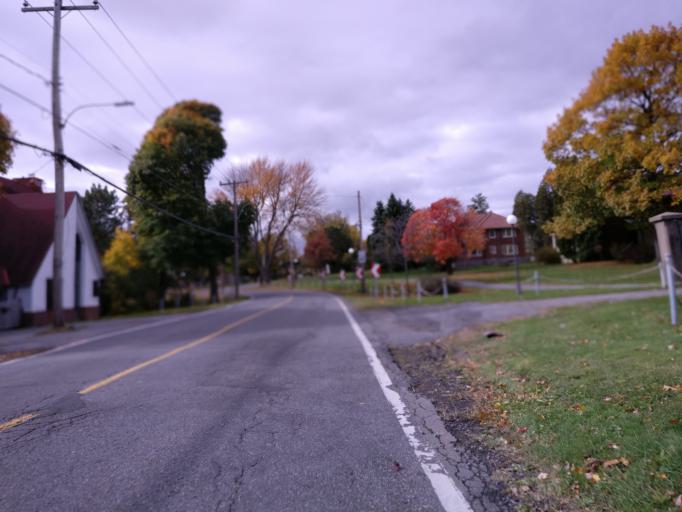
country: CA
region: Quebec
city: Sainte-Anne-de-Bellevue
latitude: 45.4051
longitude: -73.9354
